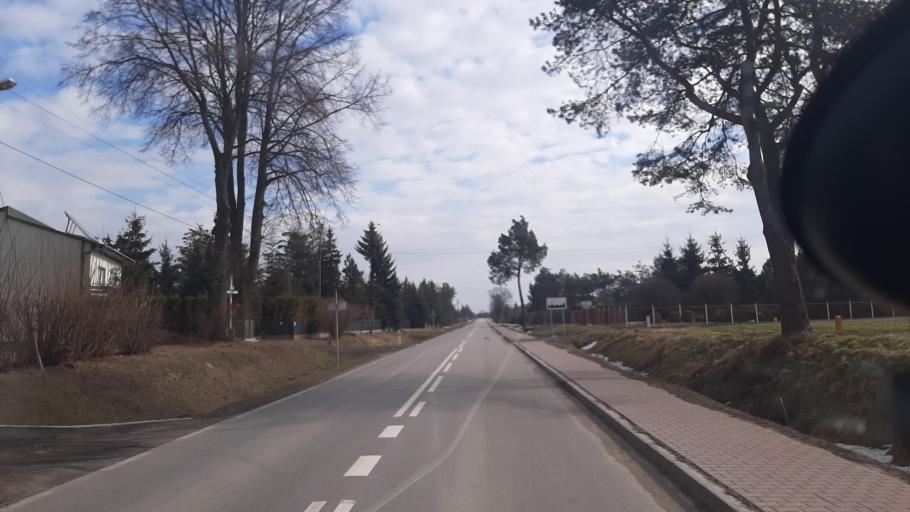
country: PL
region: Lublin Voivodeship
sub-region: Powiat lubelski
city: Niemce
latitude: 51.3615
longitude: 22.5960
